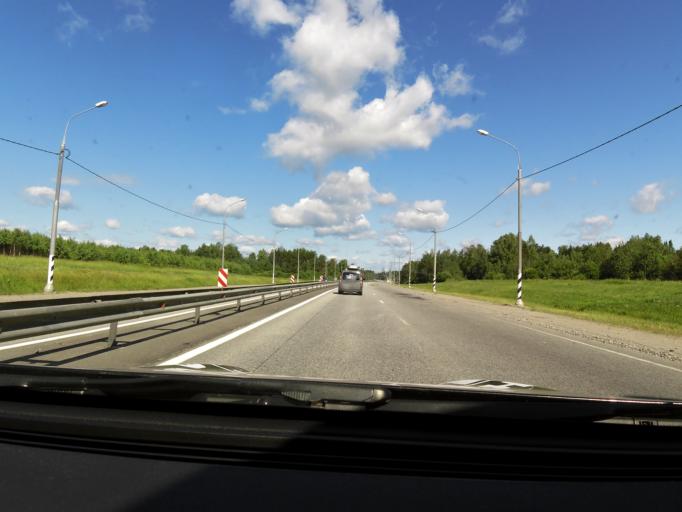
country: RU
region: Tverskaya
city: Likhoslavl'
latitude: 56.9311
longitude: 35.5208
